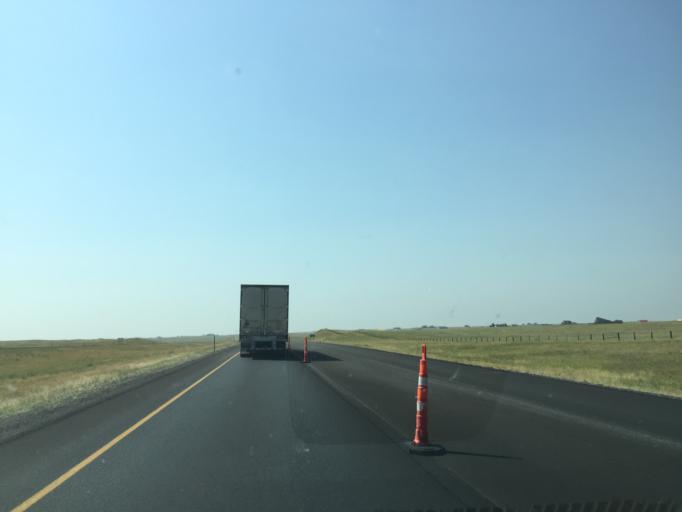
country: US
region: Wyoming
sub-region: Laramie County
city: Ranchettes
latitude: 41.3172
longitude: -104.8598
